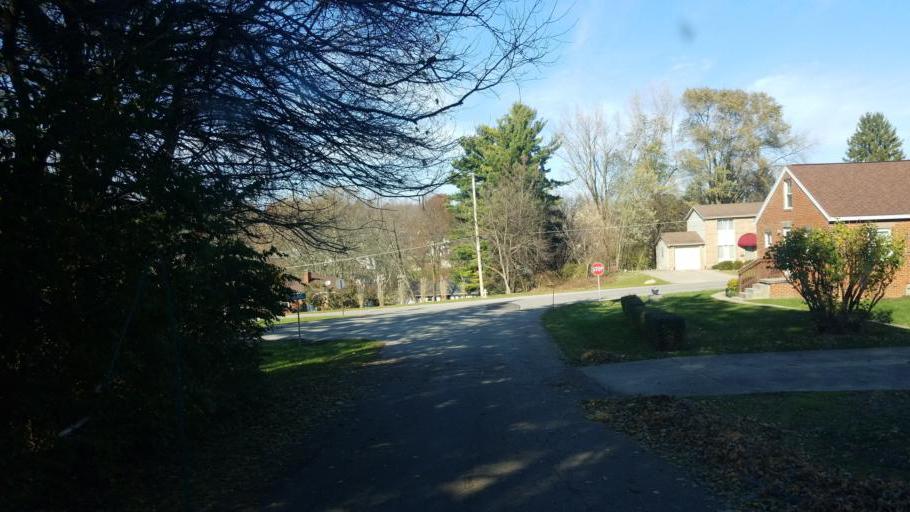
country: US
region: Ohio
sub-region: Richland County
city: Mansfield
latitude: 40.7371
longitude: -82.5154
